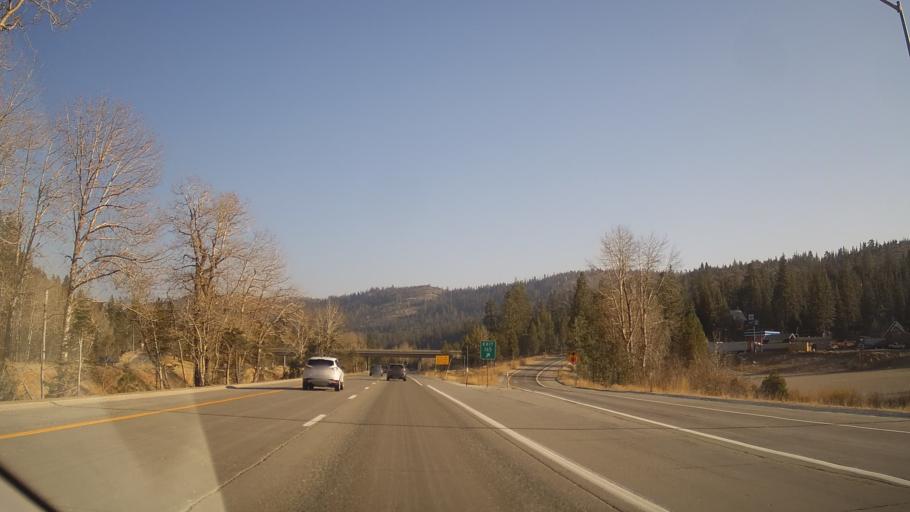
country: US
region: California
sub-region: Nevada County
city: Truckee
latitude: 39.3112
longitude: -120.5468
